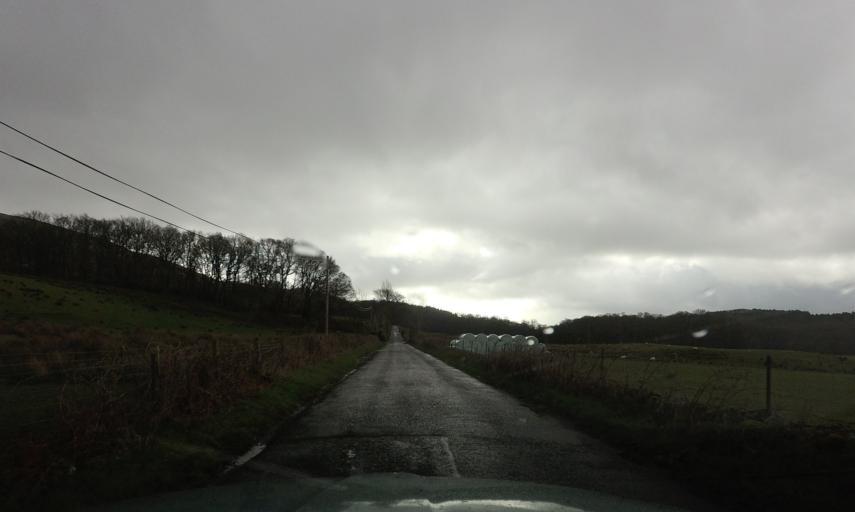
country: GB
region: Scotland
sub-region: West Dunbartonshire
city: Balloch
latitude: 56.1405
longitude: -4.6208
